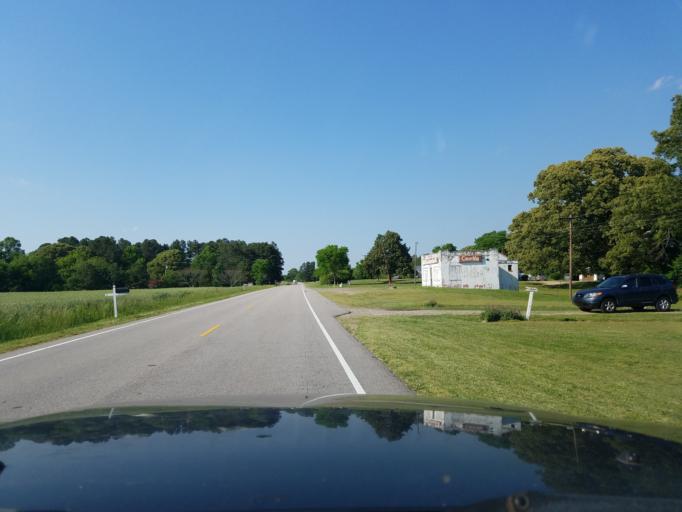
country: US
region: North Carolina
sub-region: Vance County
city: Henderson
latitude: 36.3729
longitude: -78.3713
